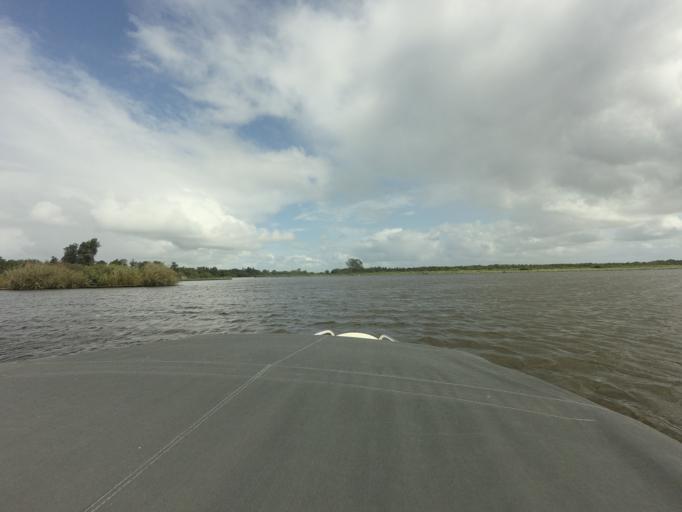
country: NL
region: Friesland
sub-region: Gemeente Boarnsterhim
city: Warten
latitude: 53.1155
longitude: 5.9332
